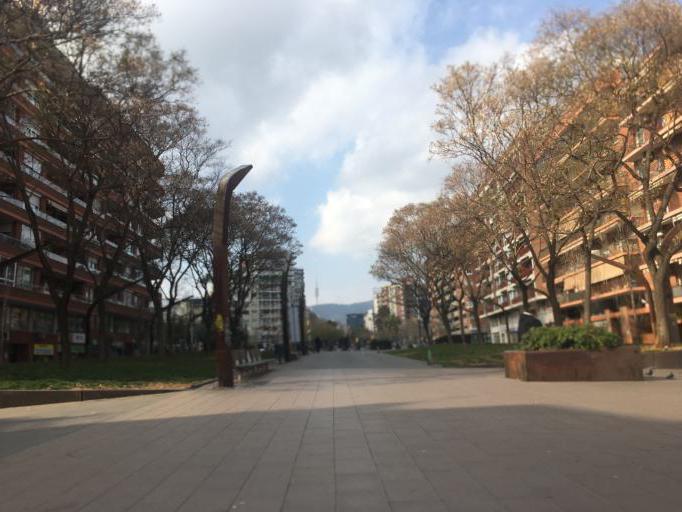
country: ES
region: Catalonia
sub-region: Provincia de Barcelona
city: les Corts
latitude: 41.3784
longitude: 2.1293
